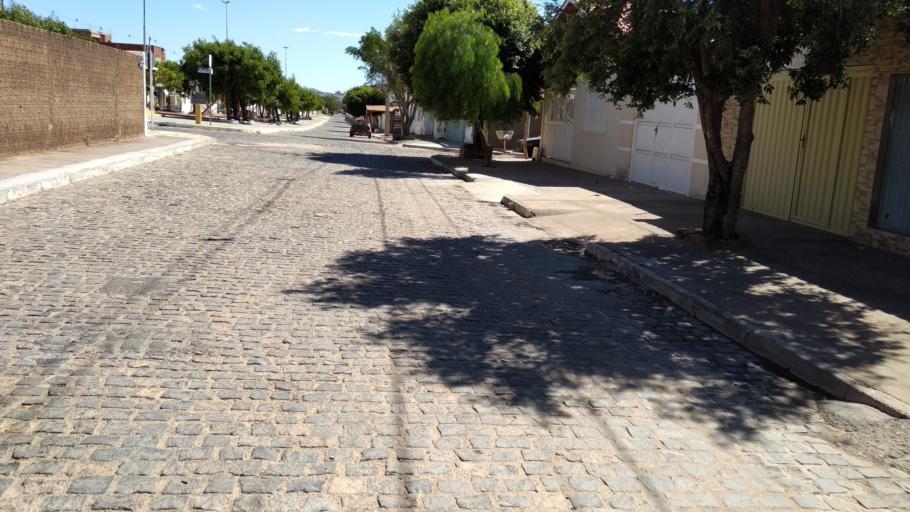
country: BR
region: Bahia
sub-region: Guanambi
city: Guanambi
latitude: -14.2364
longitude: -42.7749
